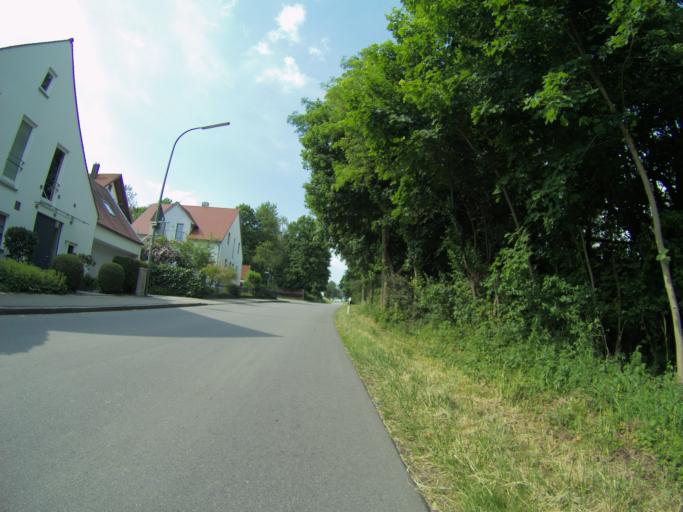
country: DE
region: Bavaria
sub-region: Upper Bavaria
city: Marzling
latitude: 48.4128
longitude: 11.7921
